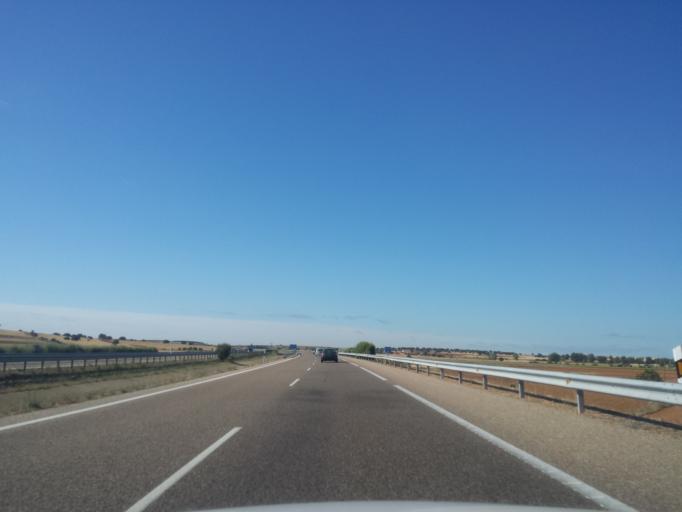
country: ES
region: Castille and Leon
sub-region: Provincia de Leon
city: Villamandos
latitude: 42.1706
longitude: -5.6346
